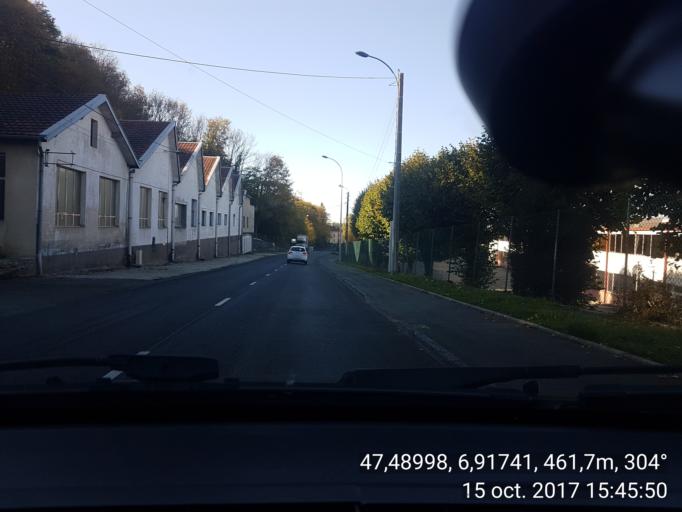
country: FR
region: Franche-Comte
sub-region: Territoire de Belfort
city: Beaucourt
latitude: 47.4900
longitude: 6.9174
